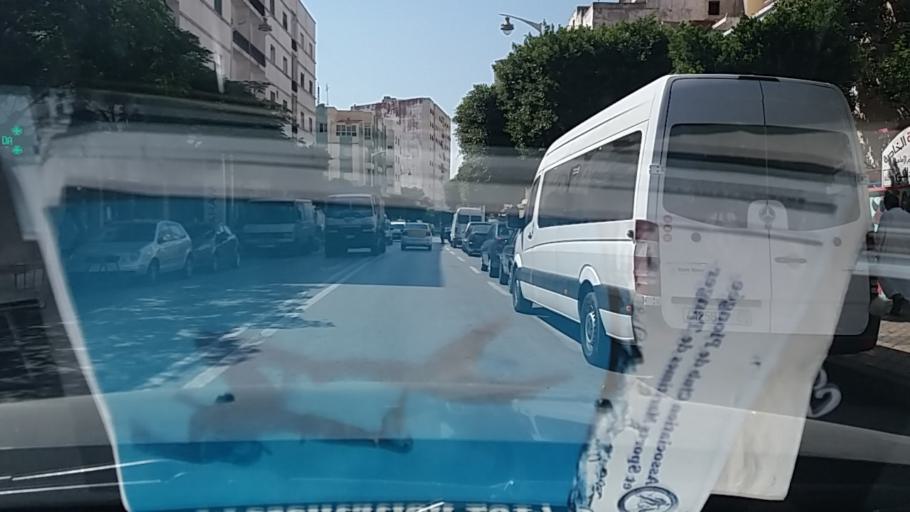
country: MA
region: Tanger-Tetouan
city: Tetouan
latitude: 35.5725
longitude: -5.3826
